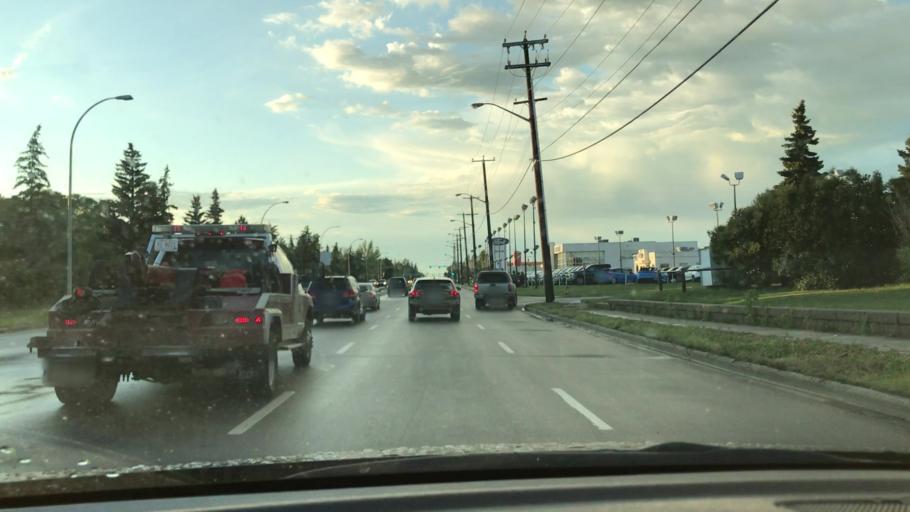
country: CA
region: Alberta
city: Edmonton
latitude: 53.5094
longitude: -113.4427
